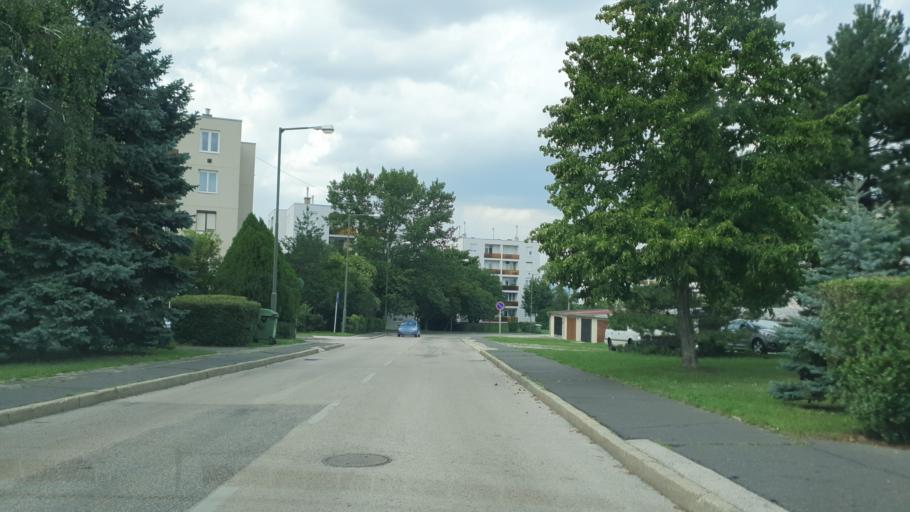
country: HU
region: Veszprem
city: Veszprem
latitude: 47.0934
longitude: 17.8963
